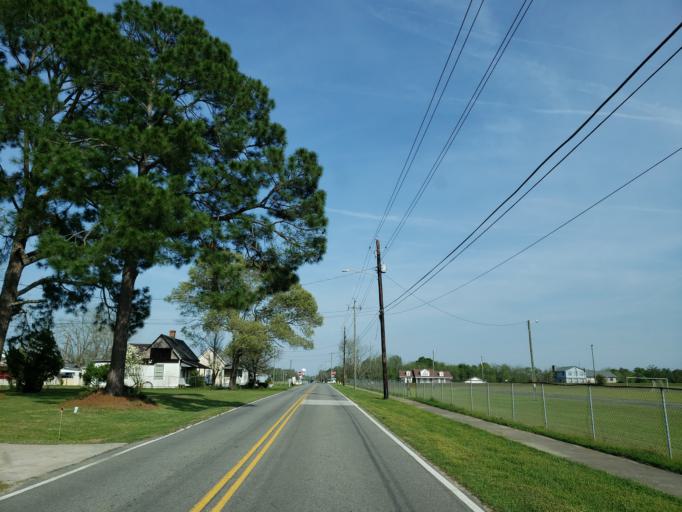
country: US
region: Georgia
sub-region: Dooly County
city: Vienna
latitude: 32.0950
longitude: -83.7835
